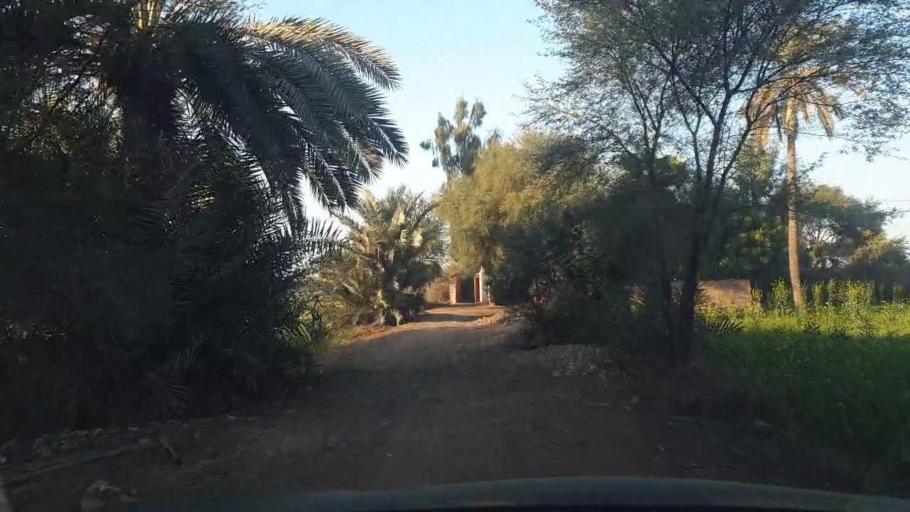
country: PK
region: Sindh
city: Ghotki
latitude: 28.0686
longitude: 69.3555
